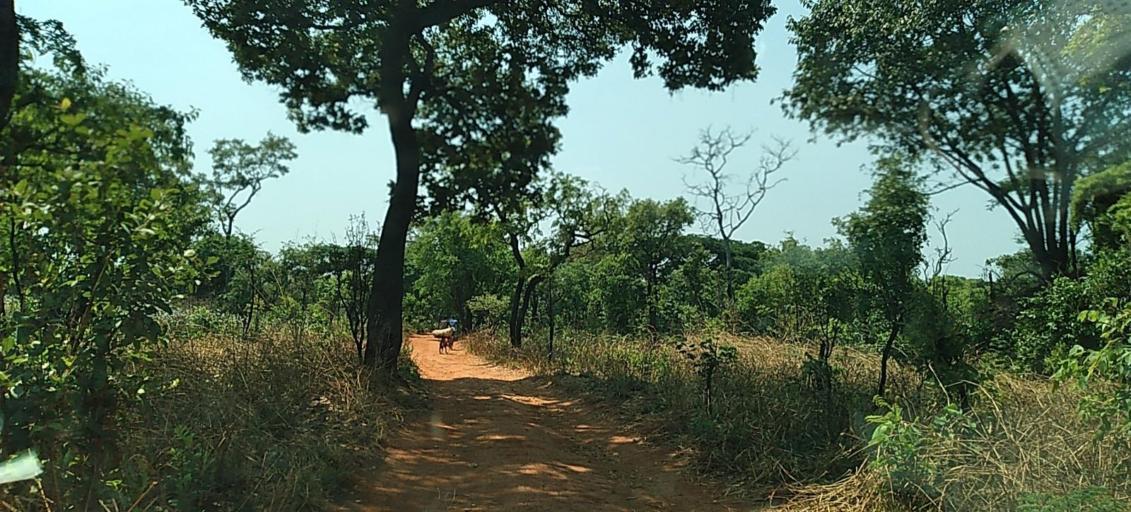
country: ZM
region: North-Western
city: Solwezi
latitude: -12.1242
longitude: 26.3050
